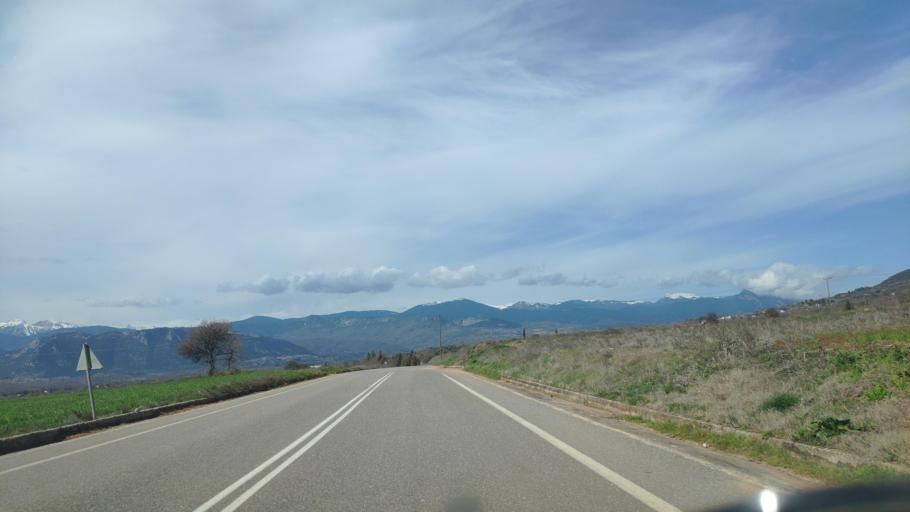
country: GR
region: Central Greece
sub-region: Nomos Fthiotidos
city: Amfikleia
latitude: 38.7100
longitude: 22.4833
